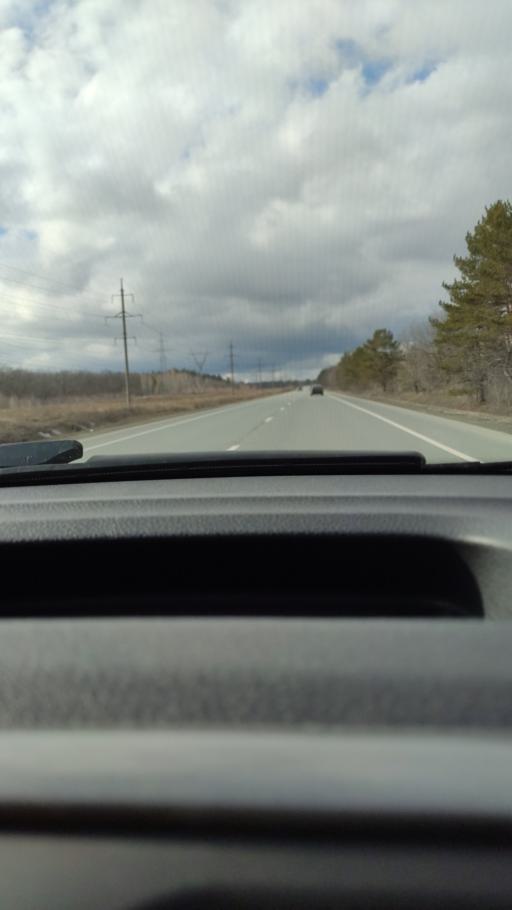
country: RU
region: Samara
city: Bogatyr'
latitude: 53.5030
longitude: 49.9458
